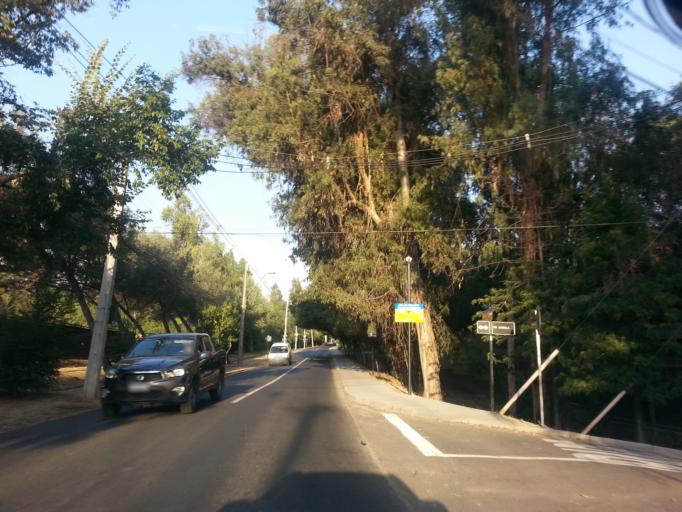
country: CL
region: Santiago Metropolitan
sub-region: Provincia de Santiago
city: Villa Presidente Frei, Nunoa, Santiago, Chile
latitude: -33.3675
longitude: -70.5527
